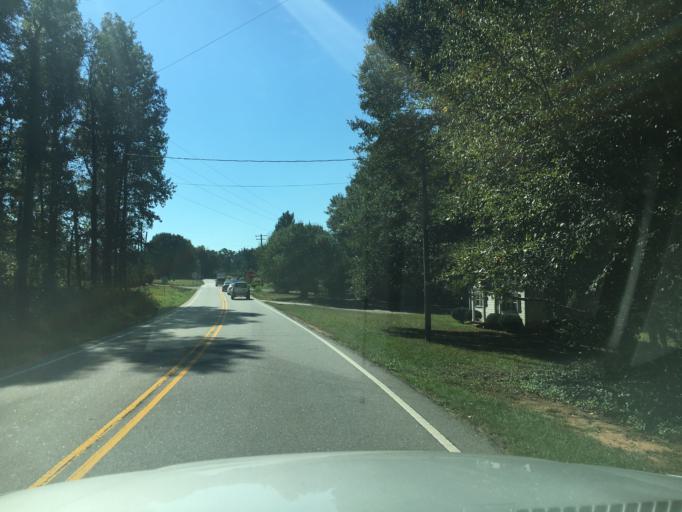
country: US
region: South Carolina
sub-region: Greenville County
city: Taylors
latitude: 34.8775
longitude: -82.2831
